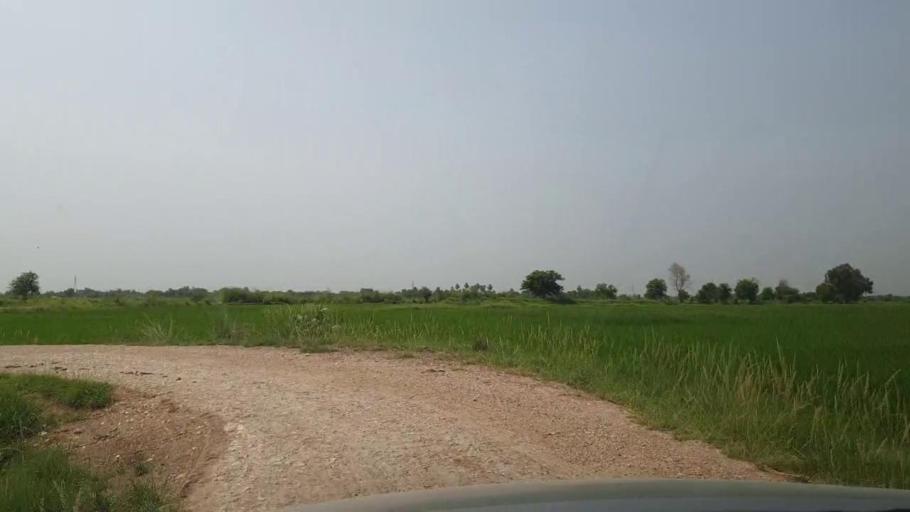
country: PK
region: Sindh
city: Madeji
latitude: 27.7939
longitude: 68.5374
